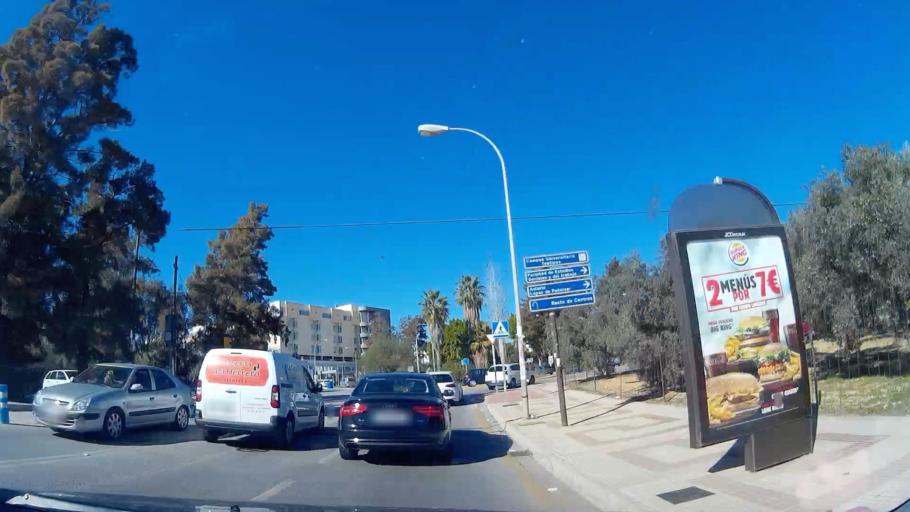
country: ES
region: Andalusia
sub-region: Provincia de Malaga
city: Malaga
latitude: 36.7168
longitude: -4.4759
